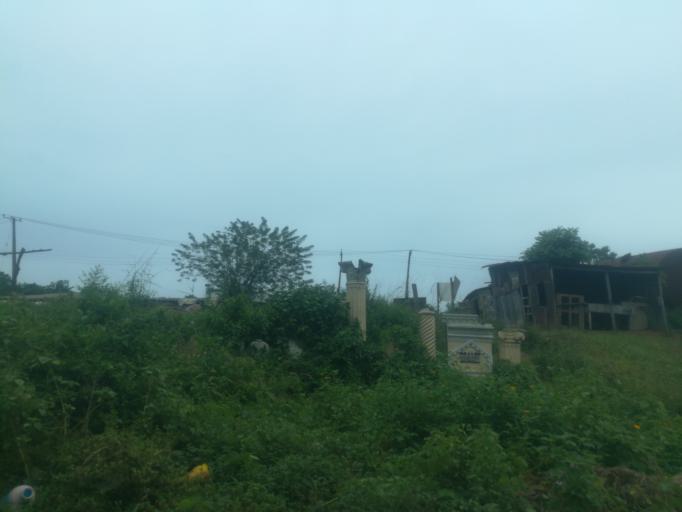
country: NG
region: Oyo
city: Ibadan
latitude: 7.3331
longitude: 3.8786
